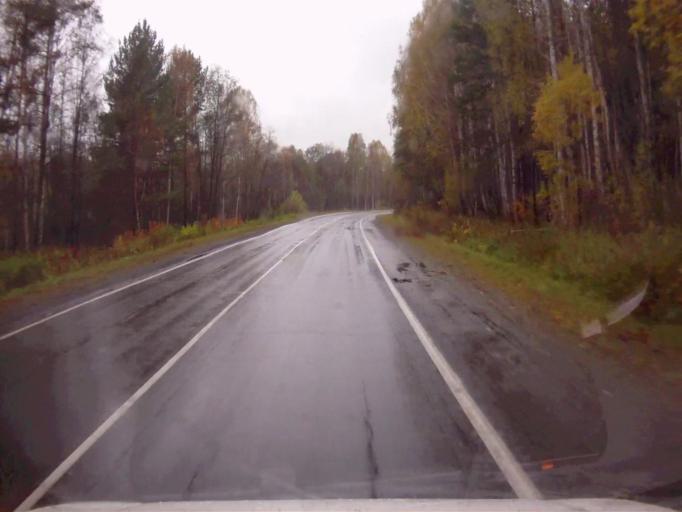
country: RU
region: Chelyabinsk
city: Verkhniy Ufaley
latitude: 55.9709
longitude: 60.3592
